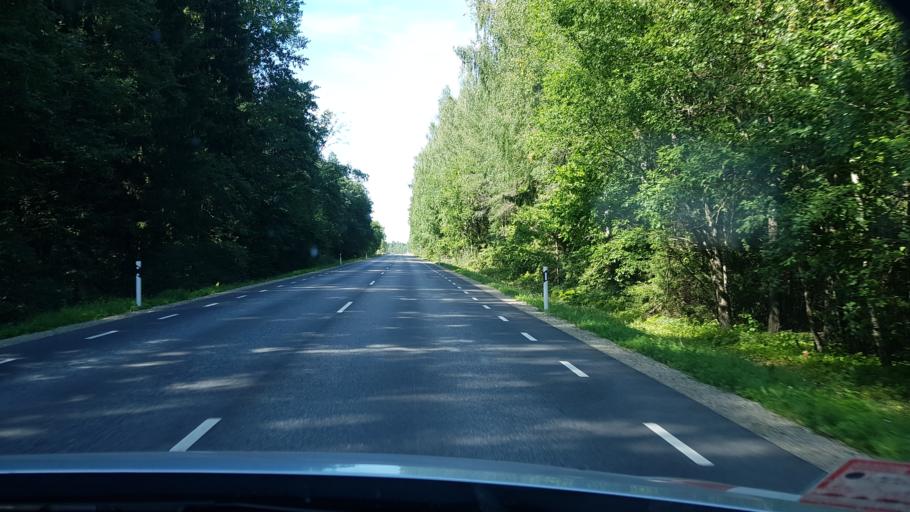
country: EE
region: Polvamaa
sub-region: Polva linn
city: Polva
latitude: 58.0310
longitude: 27.1494
